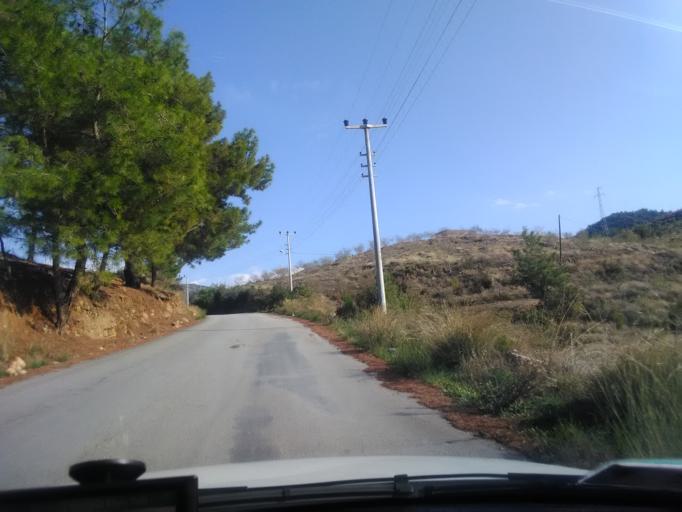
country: TR
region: Antalya
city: Gazipasa
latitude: 36.2901
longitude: 32.3263
